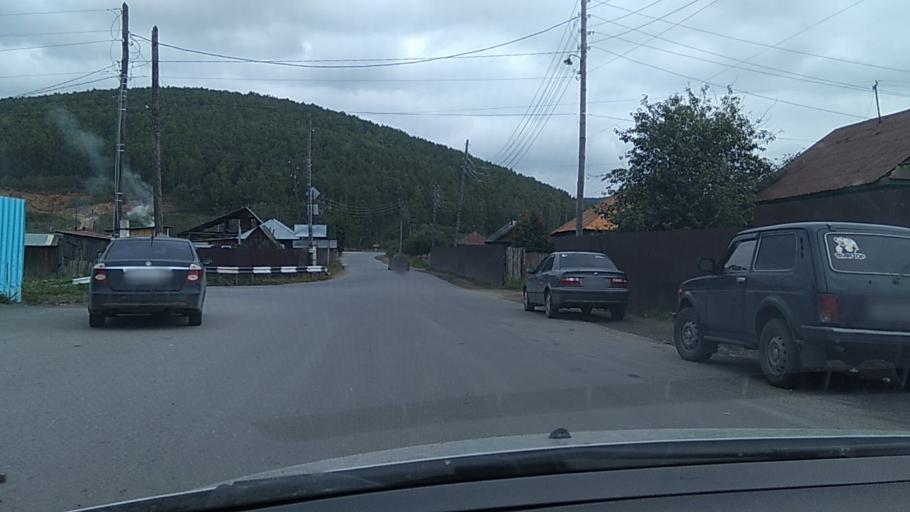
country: RU
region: Chelyabinsk
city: Zlatoust
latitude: 55.0818
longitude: 59.6913
